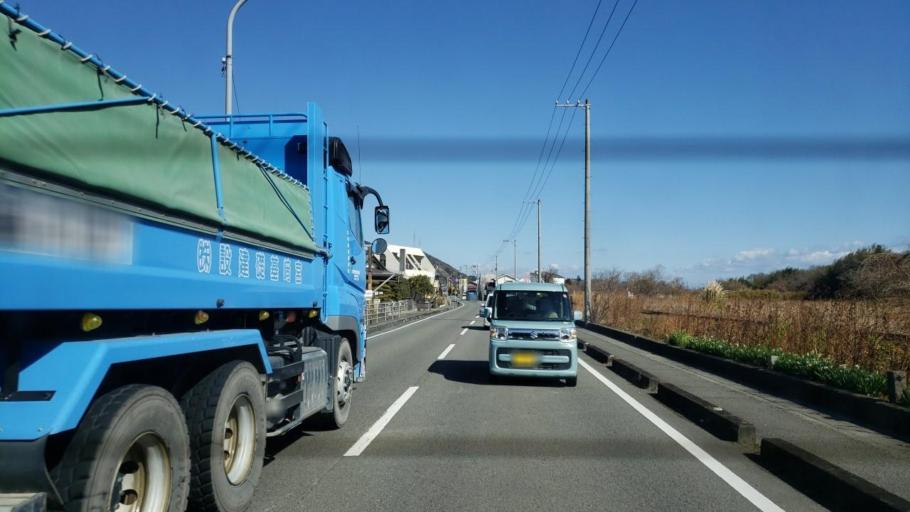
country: JP
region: Tokushima
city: Narutocho-mitsuishi
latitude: 34.1564
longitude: 134.5328
